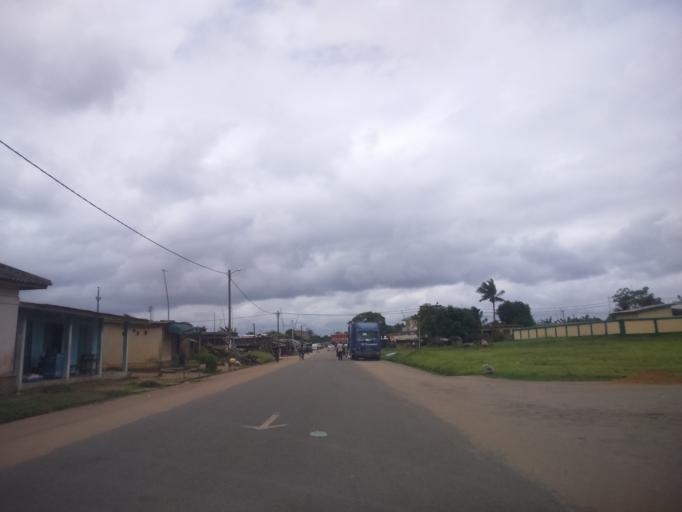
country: CI
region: Sud-Comoe
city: Adiake
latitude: 5.2877
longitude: -3.3020
